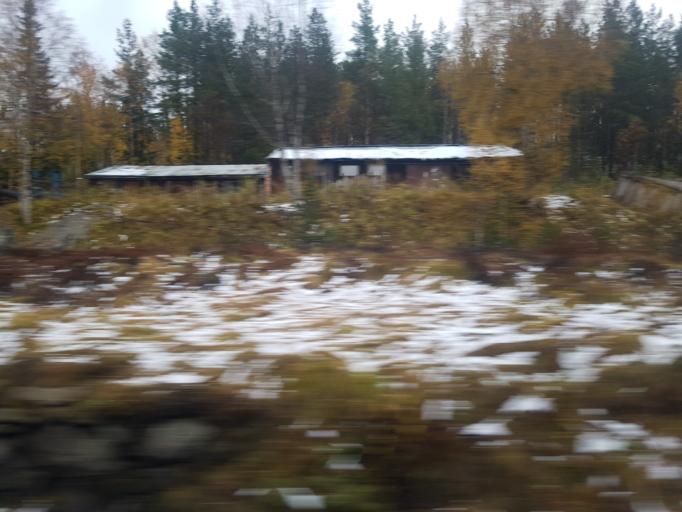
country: NO
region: Sor-Trondelag
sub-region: Rennebu
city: Berkak
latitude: 62.6806
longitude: 9.9207
